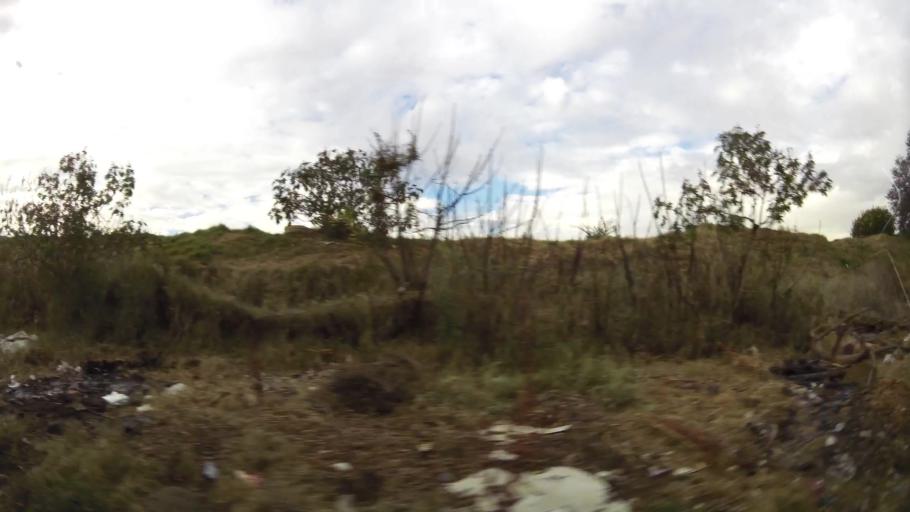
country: ZA
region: Gauteng
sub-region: City of Tshwane Metropolitan Municipality
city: Pretoria
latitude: -25.7029
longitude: 28.3017
